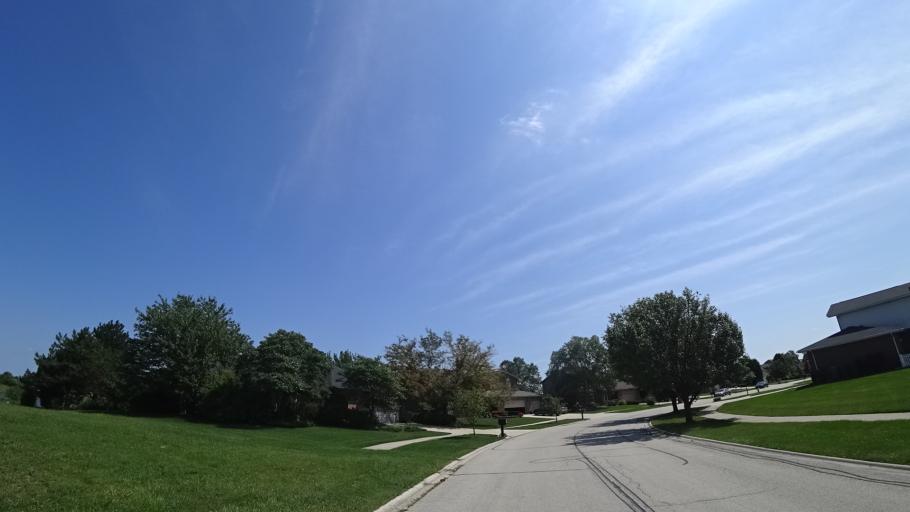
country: US
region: Illinois
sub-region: Cook County
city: Orland Hills
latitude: 41.5709
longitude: -87.8299
